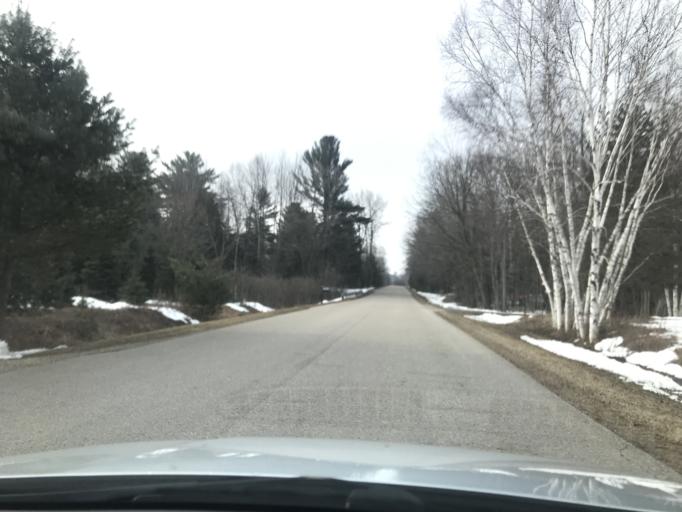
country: US
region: Wisconsin
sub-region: Oconto County
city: Oconto Falls
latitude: 44.8551
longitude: -88.1470
